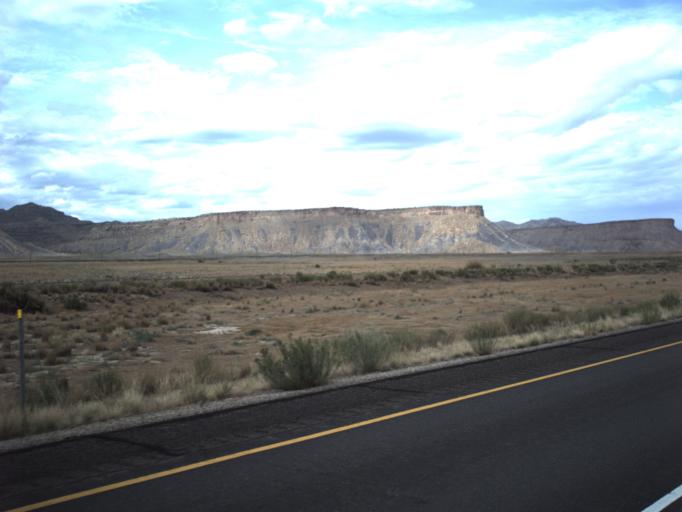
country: US
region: Utah
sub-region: Grand County
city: Moab
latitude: 38.9530
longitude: -109.7616
